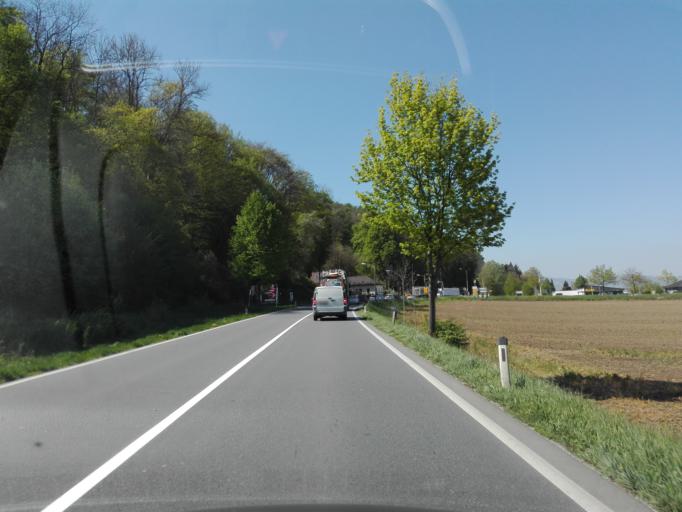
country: AT
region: Upper Austria
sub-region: Politischer Bezirk Linz-Land
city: Sankt Florian
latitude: 48.2406
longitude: 14.3638
